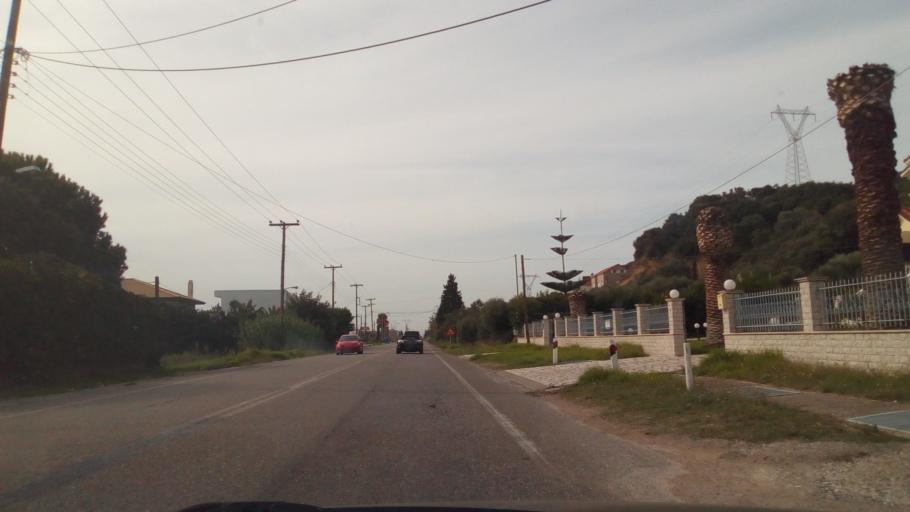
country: GR
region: West Greece
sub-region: Nomos Aitolias kai Akarnanias
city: Antirrio
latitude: 38.3582
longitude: 21.7758
